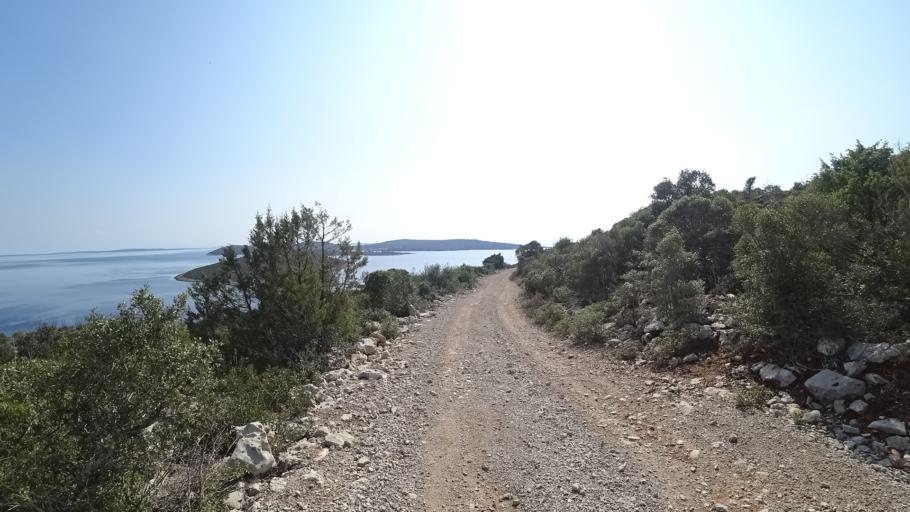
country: HR
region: Primorsko-Goranska
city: Mali Losinj
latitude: 44.4849
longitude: 14.5370
